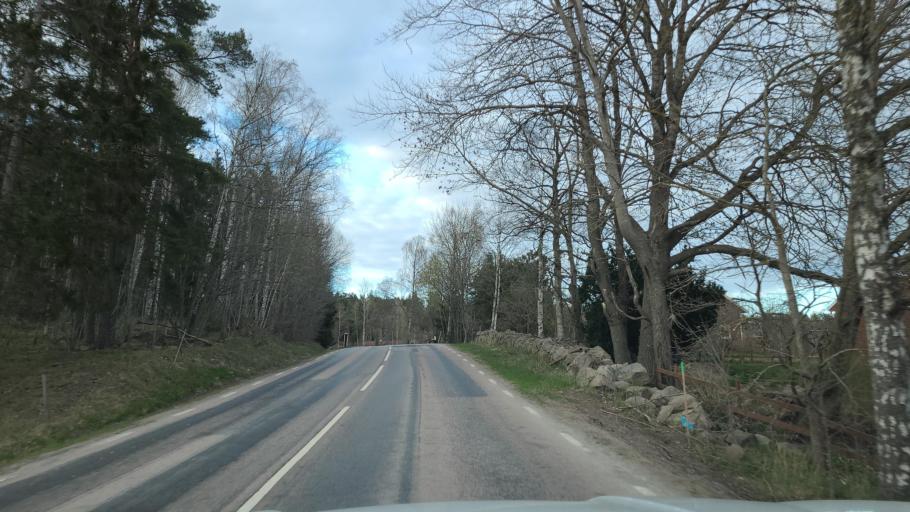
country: SE
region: Soedermanland
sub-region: Nykopings Kommun
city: Olstorp
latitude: 58.6826
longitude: 16.6356
